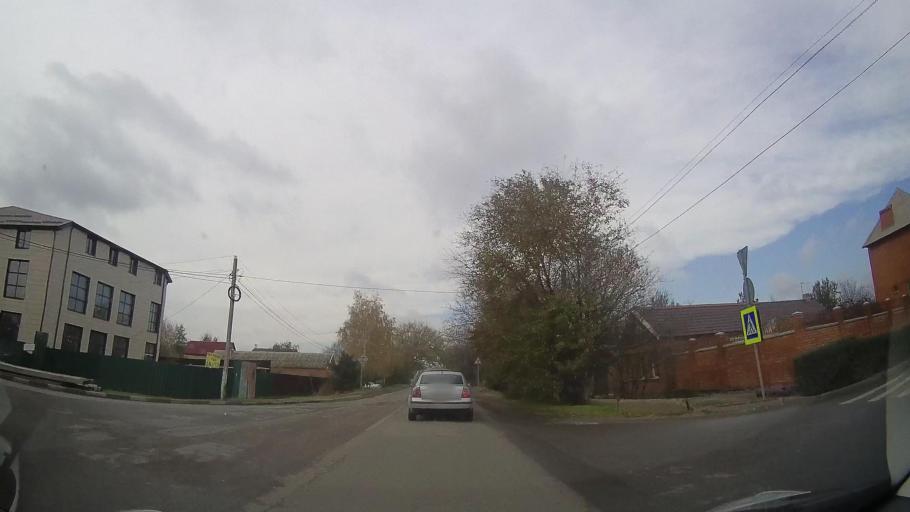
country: RU
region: Rostov
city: Bataysk
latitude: 47.1522
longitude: 39.7619
